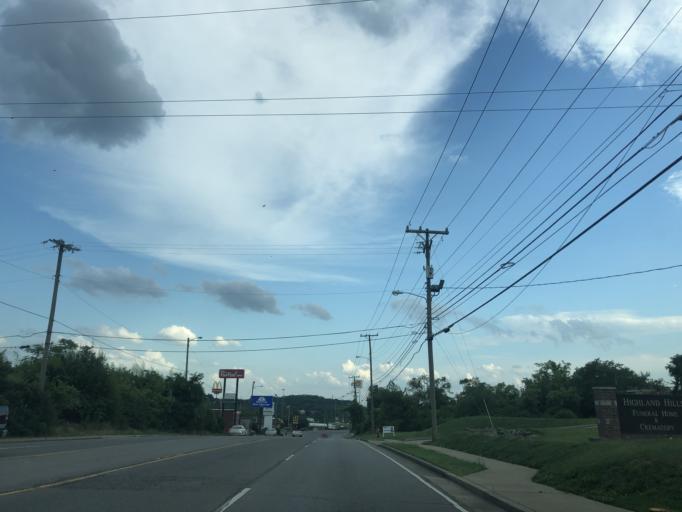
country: US
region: Tennessee
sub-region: Davidson County
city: Nashville
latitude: 36.2111
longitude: -86.7786
